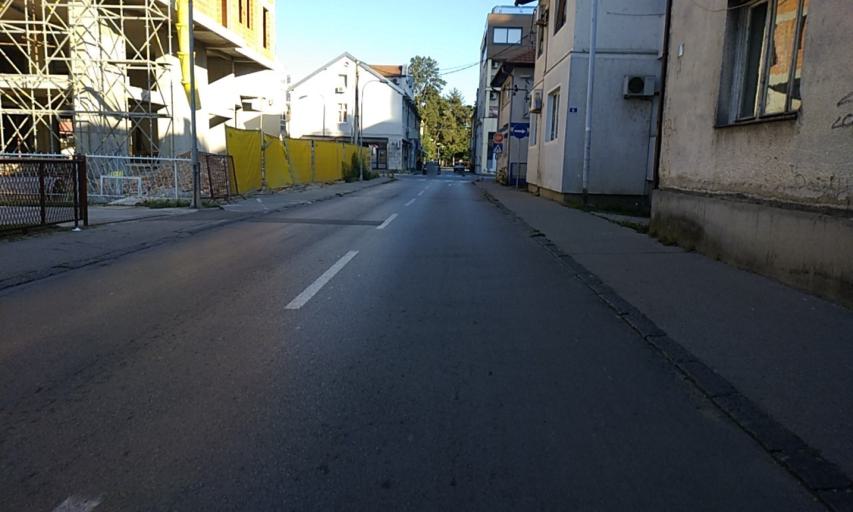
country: BA
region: Republika Srpska
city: Banja Luka
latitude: 44.7781
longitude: 17.1943
